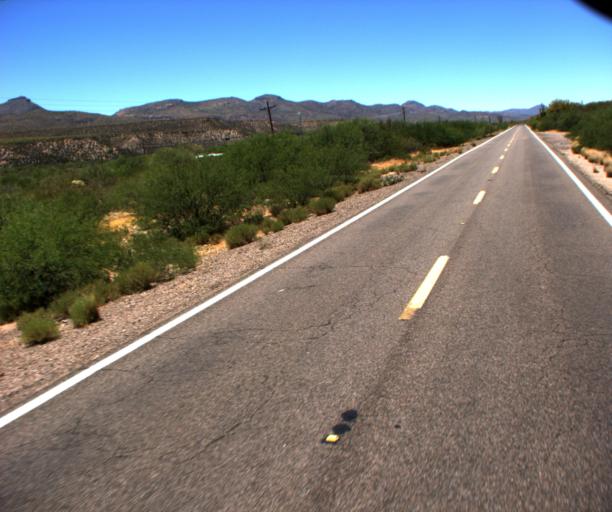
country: US
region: Arizona
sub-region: Pinal County
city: Kearny
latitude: 33.1054
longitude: -110.7529
